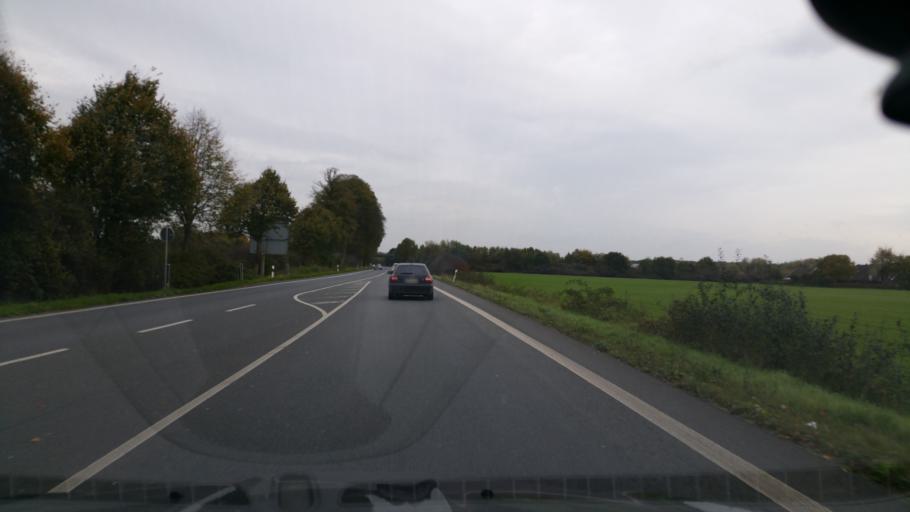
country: DE
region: North Rhine-Westphalia
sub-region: Regierungsbezirk Dusseldorf
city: Hamminkeln
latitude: 51.7500
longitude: 6.5900
